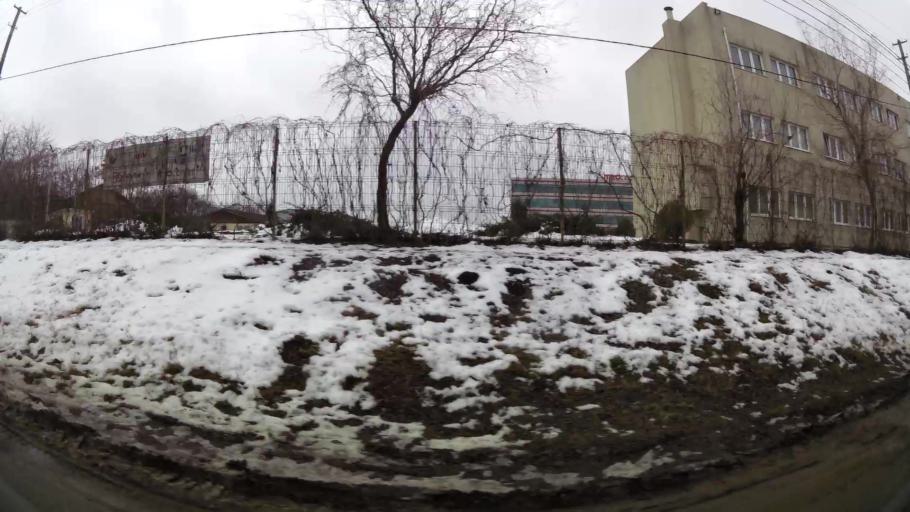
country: RO
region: Ilfov
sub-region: Comuna Chitila
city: Chitila
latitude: 44.4979
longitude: 26.0066
